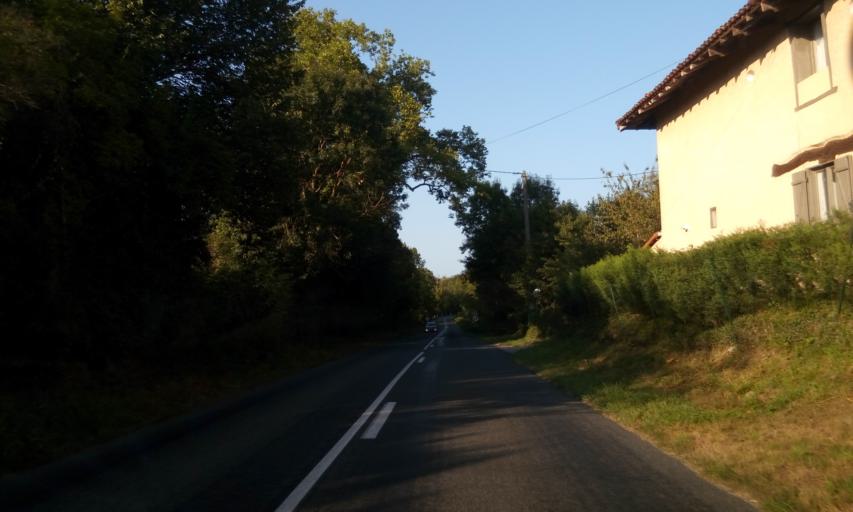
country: FR
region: Rhone-Alpes
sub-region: Departement de l'Ain
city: Chalamont
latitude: 45.9821
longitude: 5.1069
